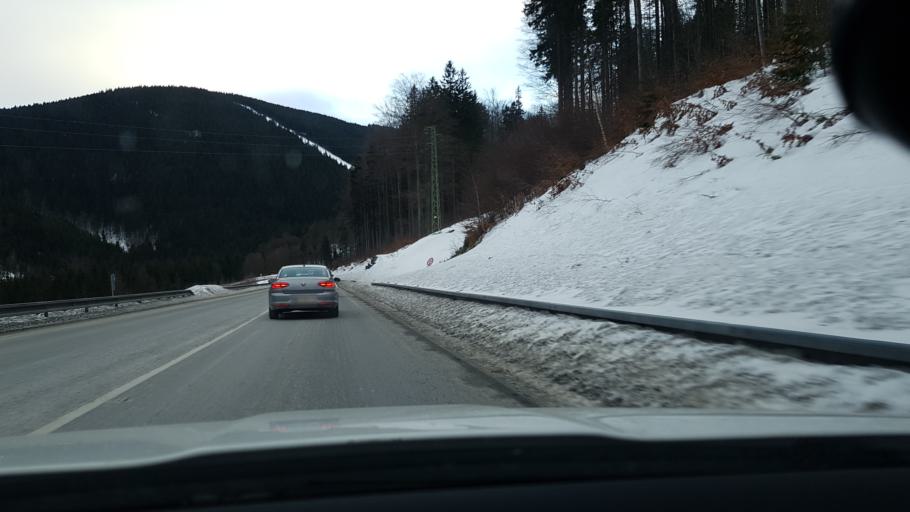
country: CZ
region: Olomoucky
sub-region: Okres Sumperk
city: Loucna nad Desnou
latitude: 50.1371
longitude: 17.1628
